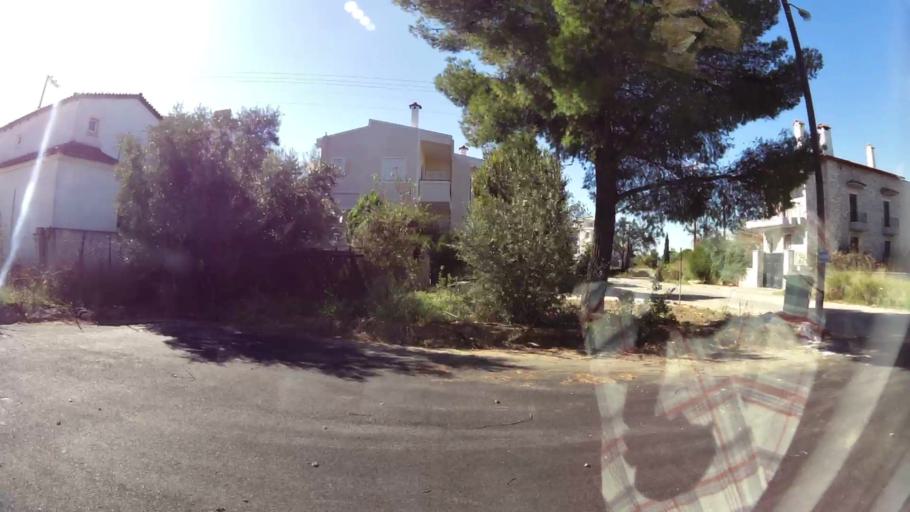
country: GR
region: Attica
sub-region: Nomarchia Athinas
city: Lykovrysi
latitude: 38.0942
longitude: 23.7888
